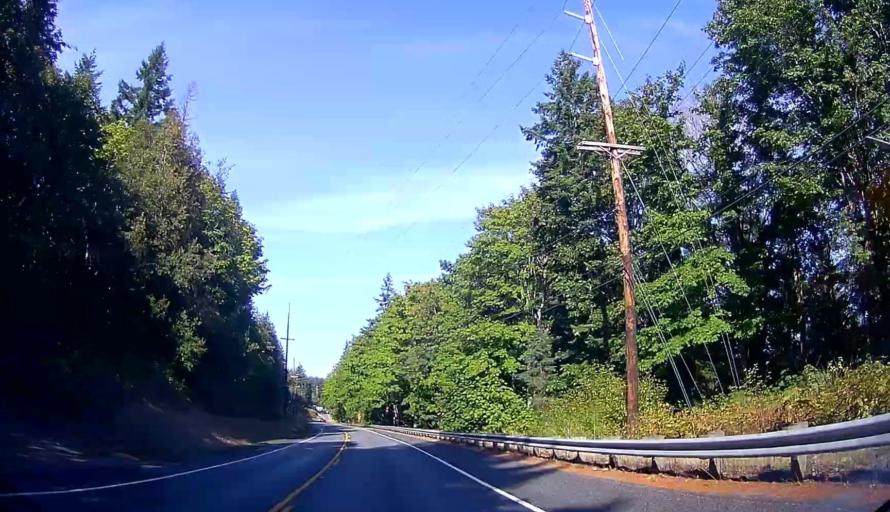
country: US
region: Washington
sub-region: Island County
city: Camano
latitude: 48.2073
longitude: -122.4804
